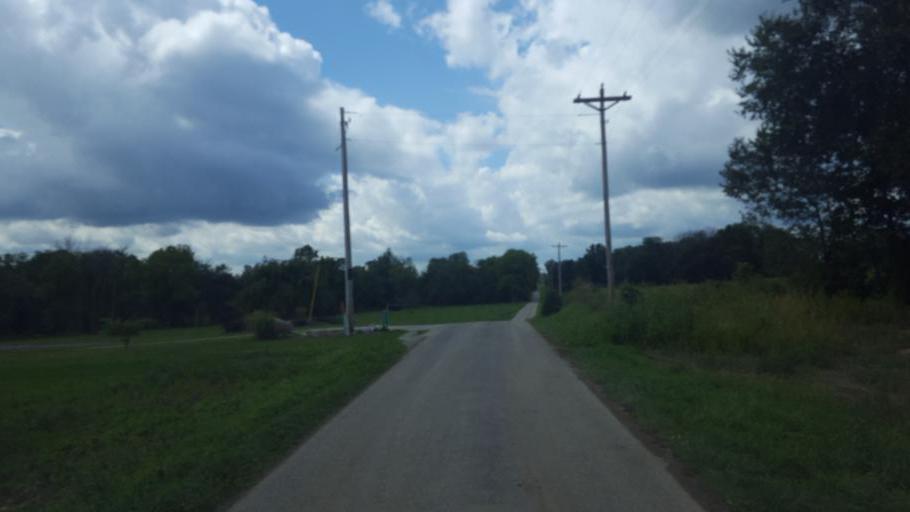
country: US
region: Ohio
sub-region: Huron County
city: Plymouth
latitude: 41.0782
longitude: -82.6351
